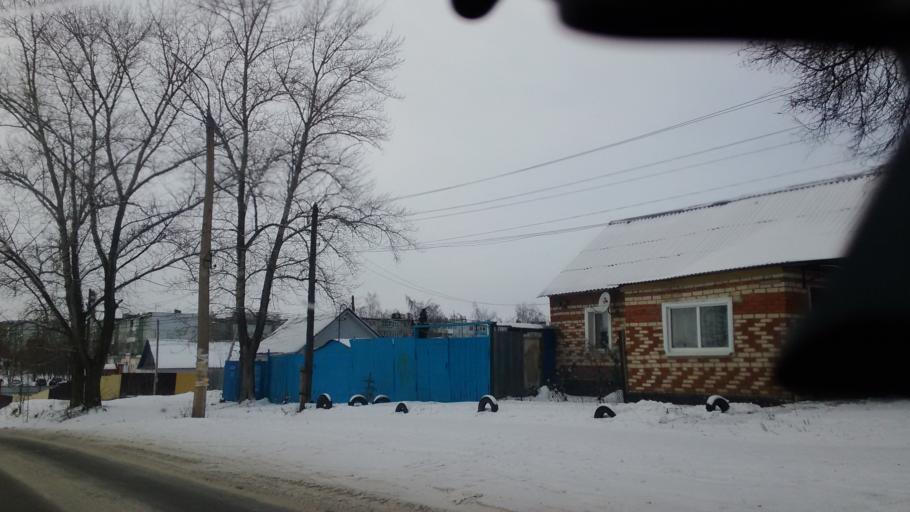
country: RU
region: Tula
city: Bogoroditsk
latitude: 53.7678
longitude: 38.1167
